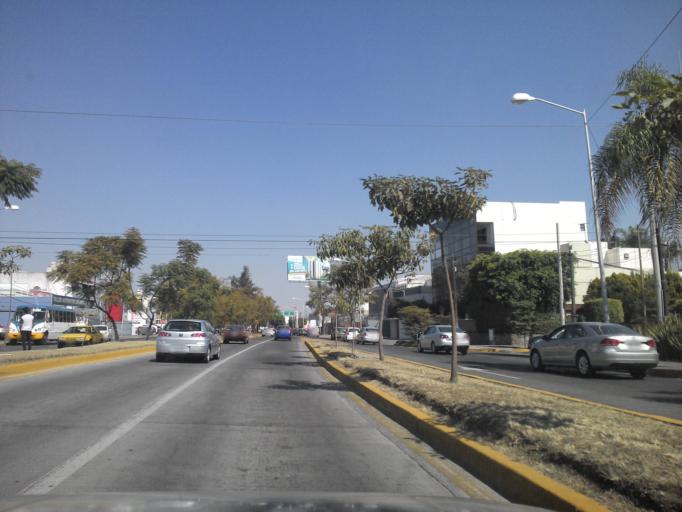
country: MX
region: Jalisco
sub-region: Zapopan
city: Zapopan
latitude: 20.6988
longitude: -103.3694
